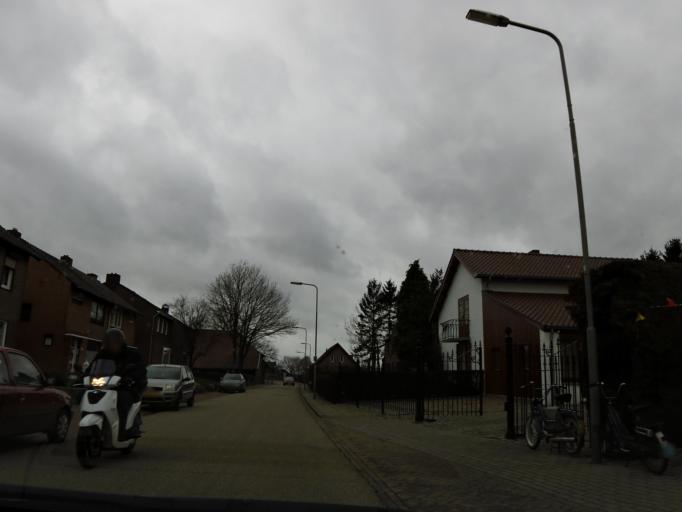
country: NL
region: Limburg
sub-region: Eijsden-Margraten
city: Margraten
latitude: 50.7878
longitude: 5.8051
